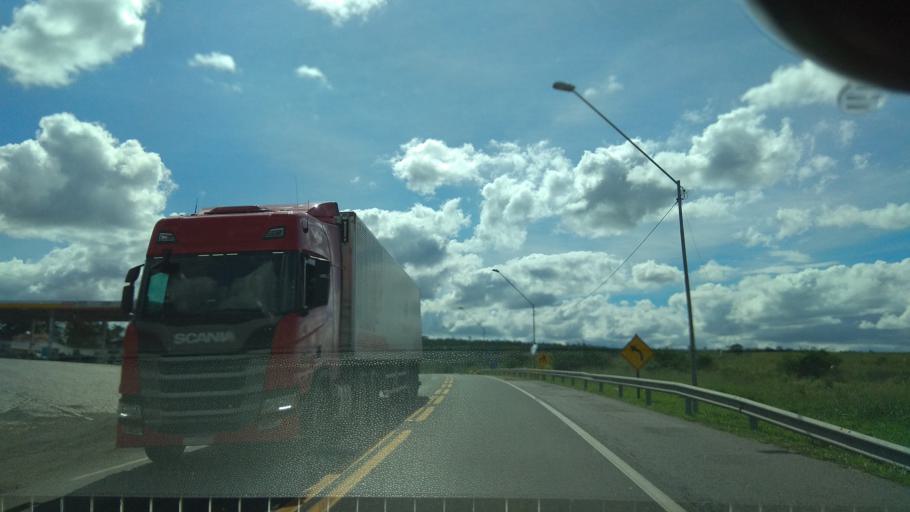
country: BR
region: Bahia
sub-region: Santa Ines
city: Santa Ines
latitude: -13.2288
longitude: -40.0173
